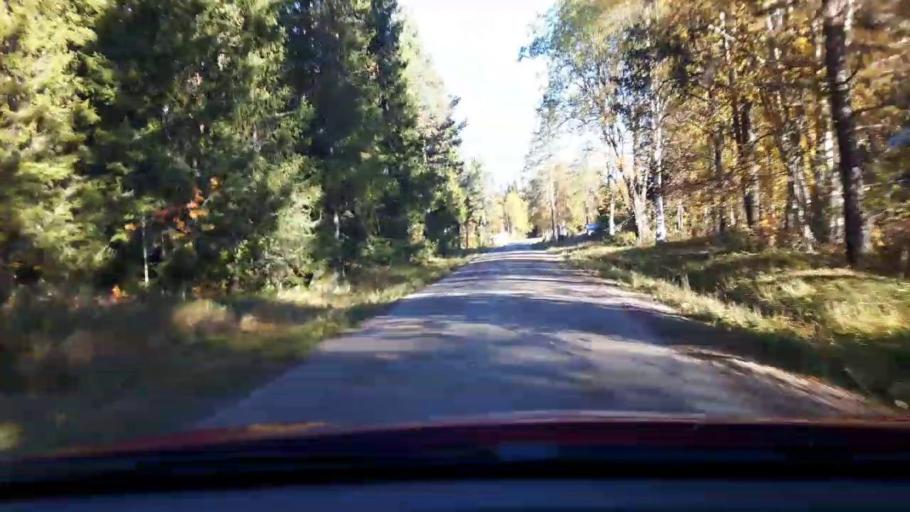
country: SE
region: Jaemtland
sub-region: Stroemsunds Kommun
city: Stroemsund
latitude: 64.3973
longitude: 15.1456
